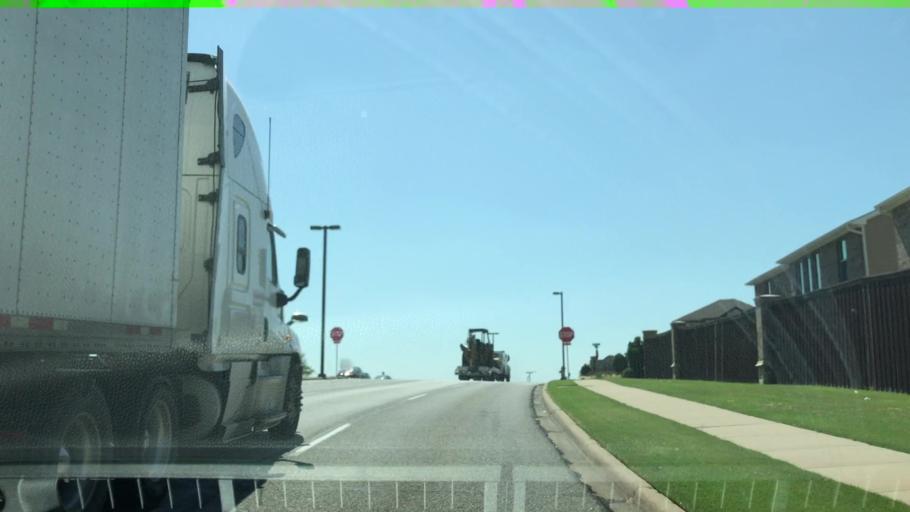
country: US
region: Texas
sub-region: Dallas County
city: Irving
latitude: 32.8655
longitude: -96.9984
